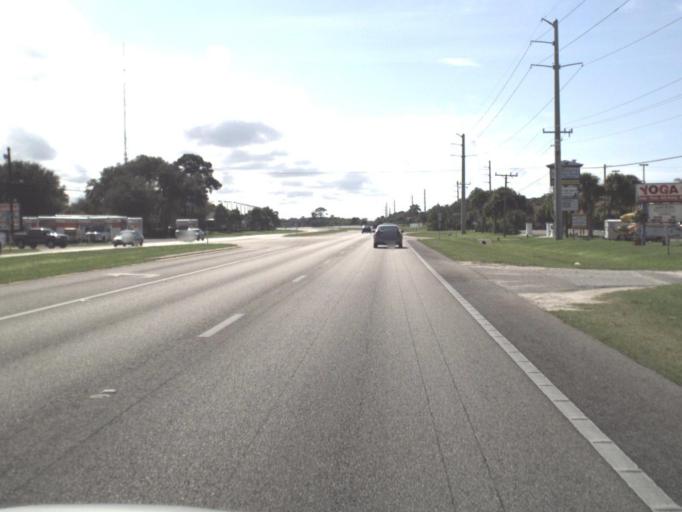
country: US
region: Florida
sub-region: Sarasota County
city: Laurel
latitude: 27.1566
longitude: -82.4702
